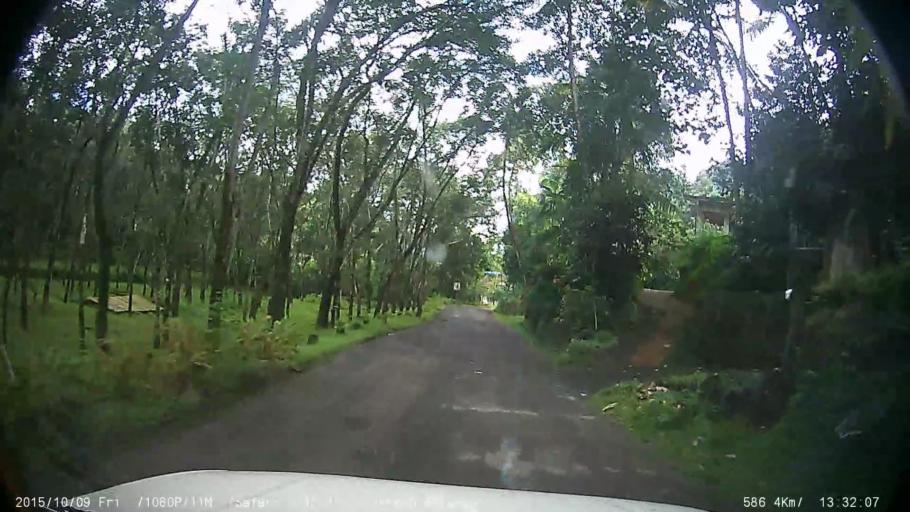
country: IN
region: Kerala
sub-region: Ernakulam
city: Ramamangalam
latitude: 9.9122
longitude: 76.5578
